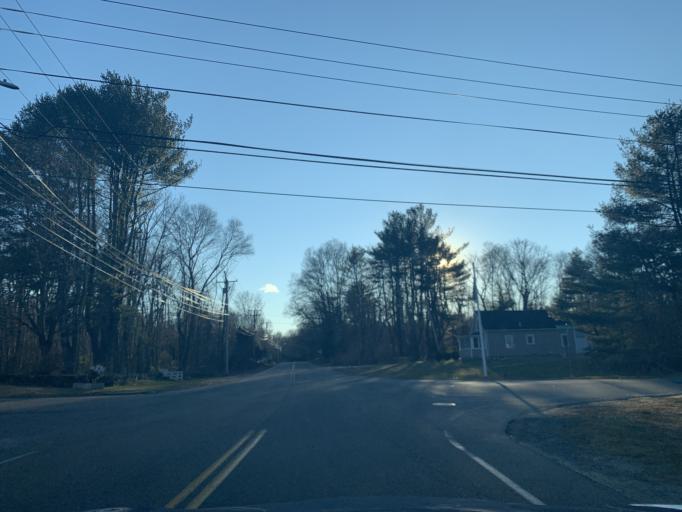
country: US
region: Massachusetts
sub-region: Bristol County
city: Rehoboth
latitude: 41.8733
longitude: -71.2311
